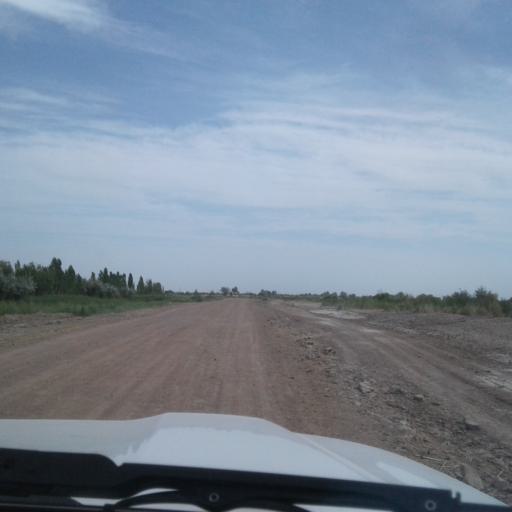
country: TM
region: Dasoguz
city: Tagta
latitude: 41.5500
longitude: 59.8124
